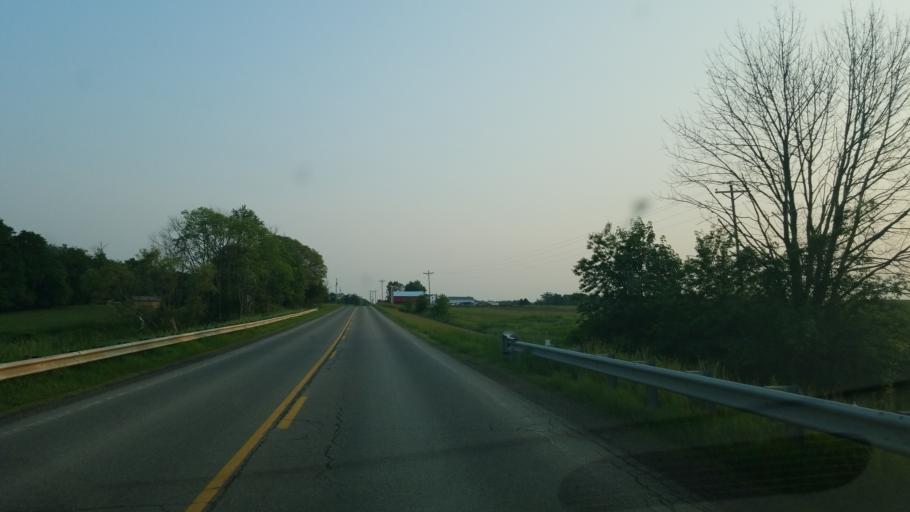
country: US
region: Ohio
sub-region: Ashland County
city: Ashland
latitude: 40.9379
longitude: -82.3898
